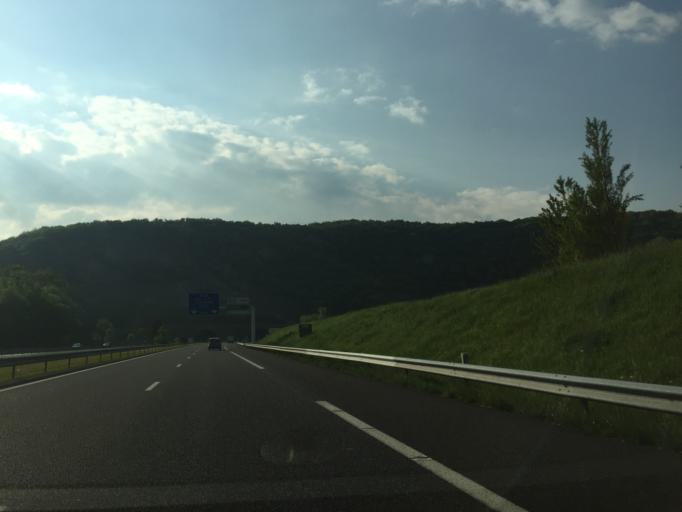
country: FR
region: Rhone-Alpes
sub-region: Departement de l'Isere
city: Allieres-et-Risset
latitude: 45.0861
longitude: 5.6722
